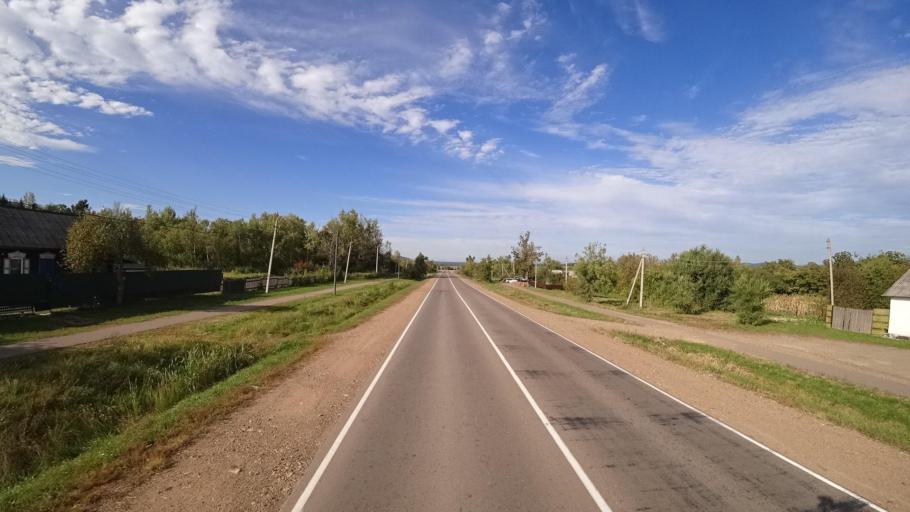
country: RU
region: Primorskiy
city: Dostoyevka
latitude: 44.3023
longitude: 133.4493
